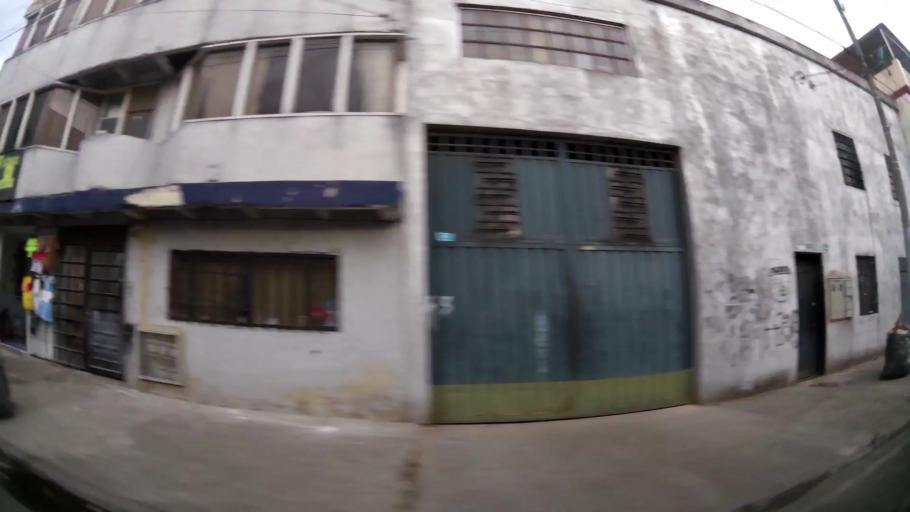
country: CO
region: Bogota D.C.
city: Barrio San Luis
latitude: 4.6735
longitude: -74.0739
